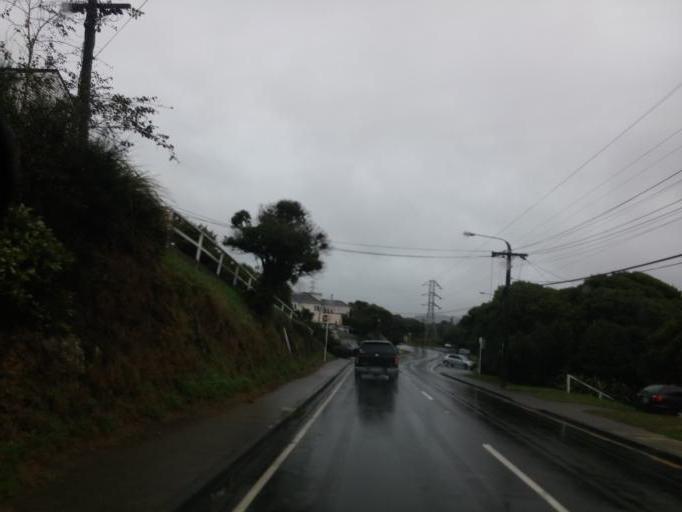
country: NZ
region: Wellington
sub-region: Wellington City
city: Kelburn
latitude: -41.2693
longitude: 174.7552
